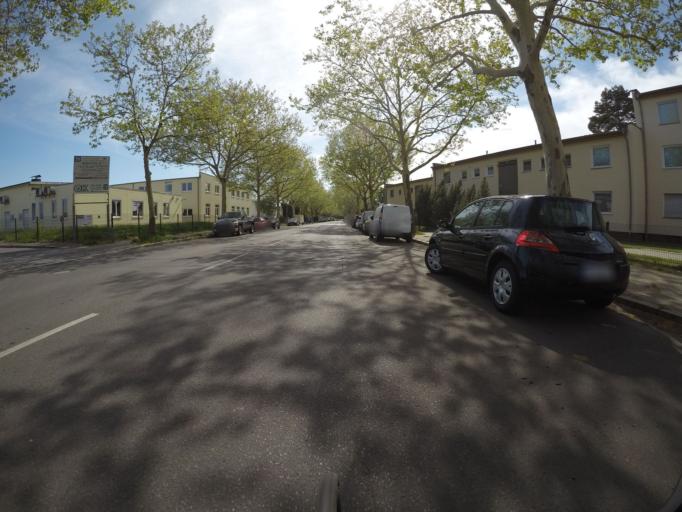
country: DE
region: Berlin
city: Marienfelde
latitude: 52.4182
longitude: 13.3877
